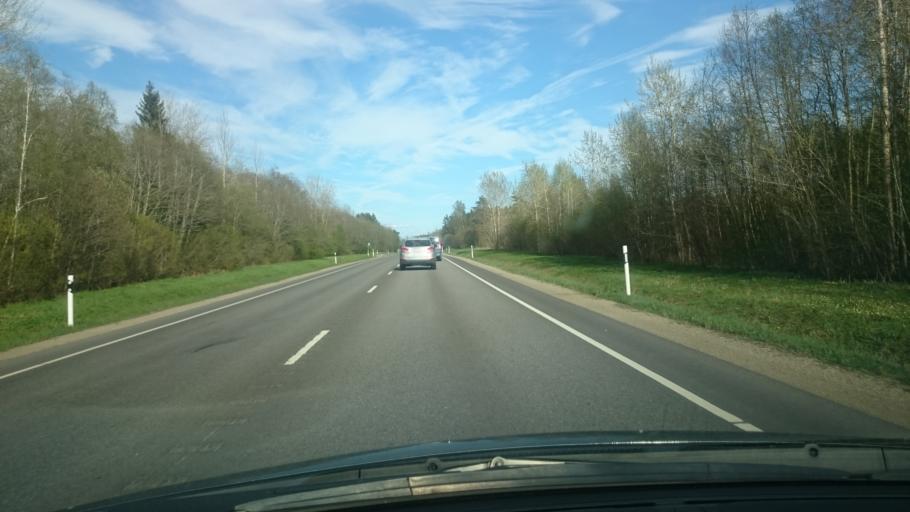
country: EE
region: Ida-Virumaa
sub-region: Toila vald
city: Voka
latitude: 59.3933
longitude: 27.6429
